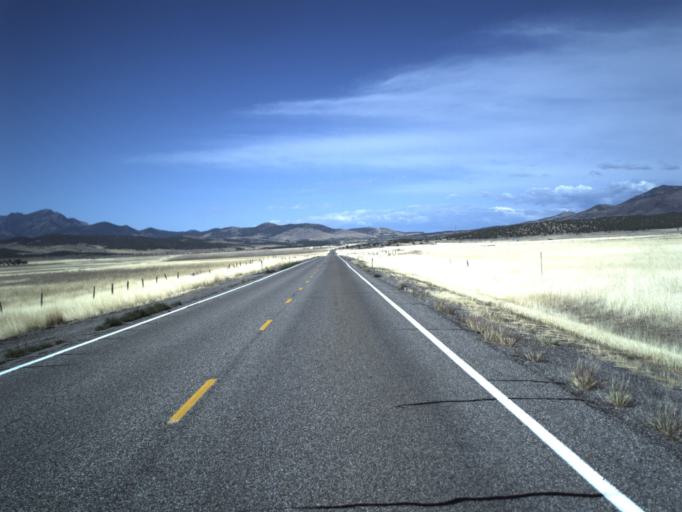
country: US
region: Utah
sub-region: Millard County
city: Fillmore
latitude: 39.1155
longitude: -112.2631
